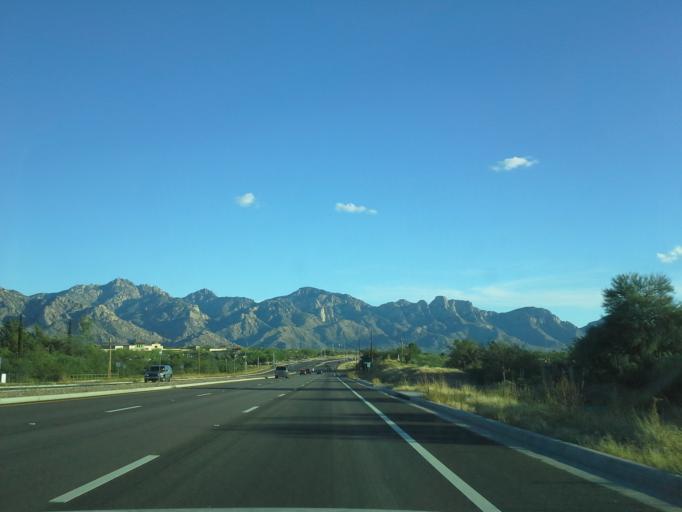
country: US
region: Arizona
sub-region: Pima County
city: Catalina
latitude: 32.4881
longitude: -110.9239
